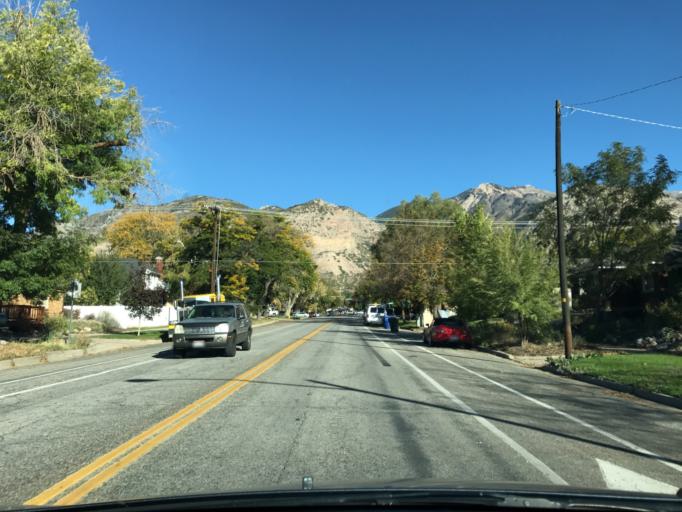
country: US
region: Utah
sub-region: Weber County
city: Ogden
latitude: 41.2183
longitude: -111.9510
